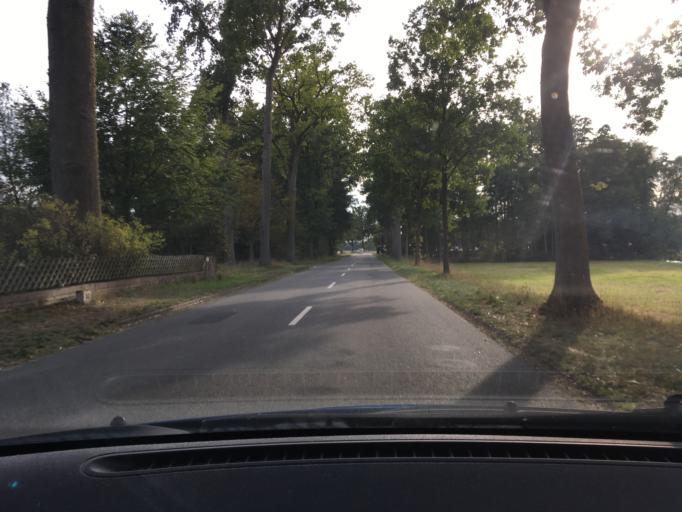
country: DE
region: Lower Saxony
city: Wietzendorf
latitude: 52.9166
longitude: 10.0530
